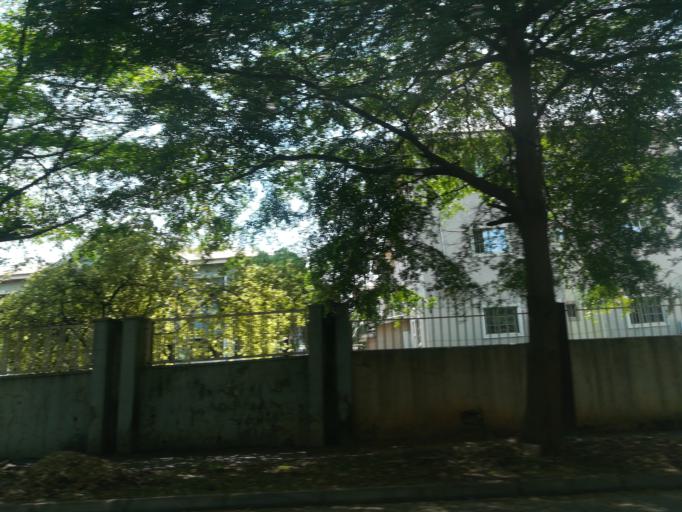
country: NG
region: Abuja Federal Capital Territory
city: Abuja
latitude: 9.0737
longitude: 7.4409
